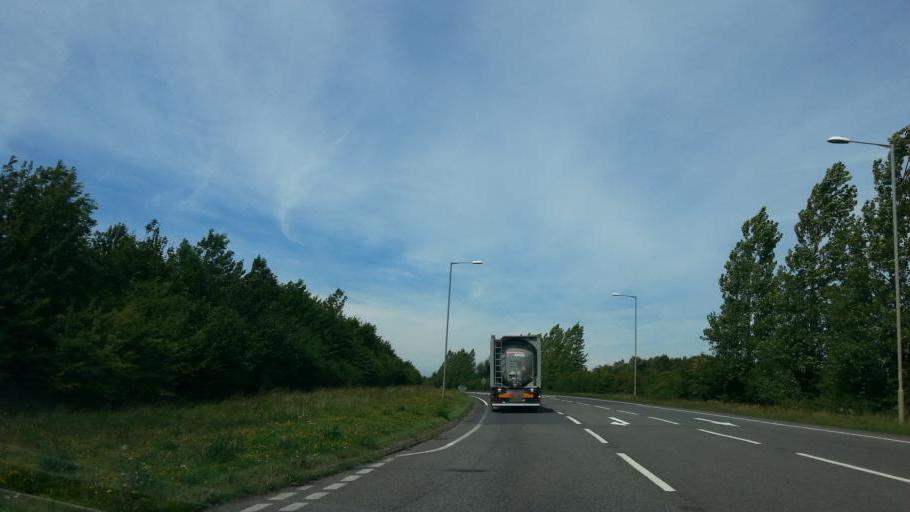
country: GB
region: England
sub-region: Cambridgeshire
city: Soham
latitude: 52.3122
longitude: 0.3702
